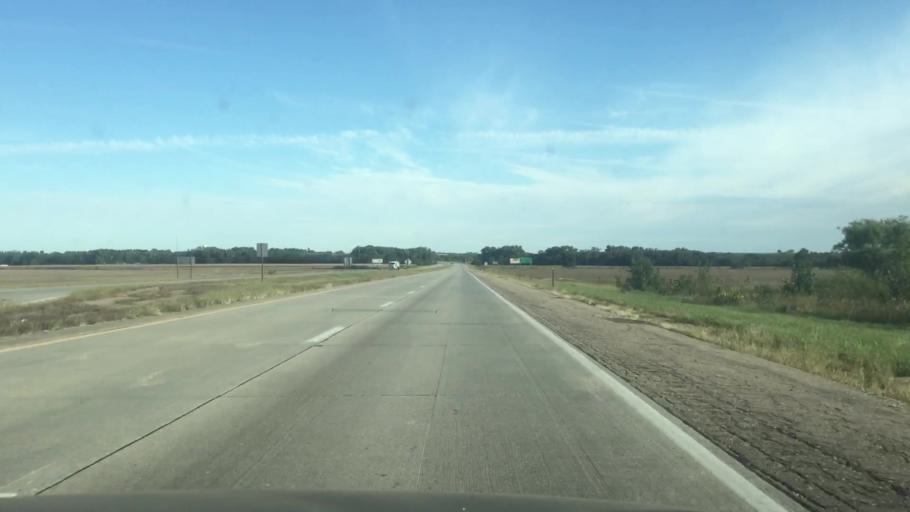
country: US
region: Nebraska
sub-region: Thayer County
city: Hebron
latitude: 40.1482
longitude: -97.5707
